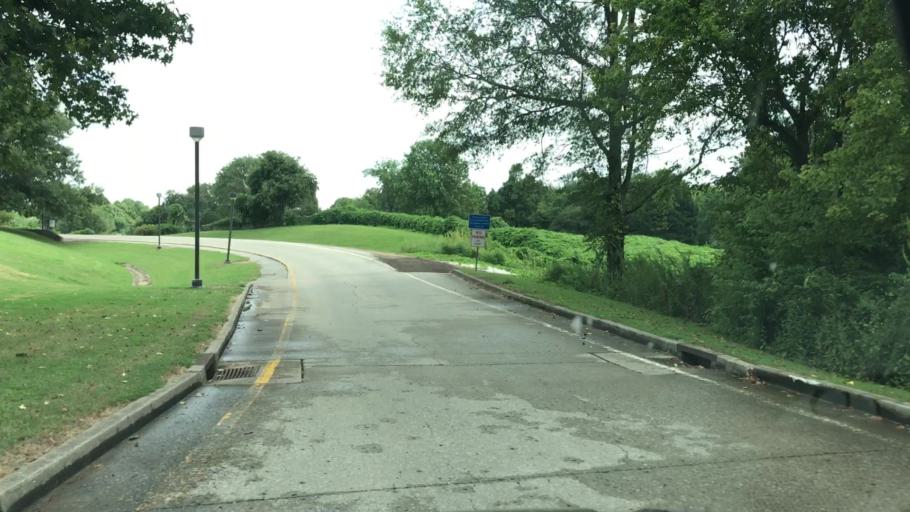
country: US
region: Tennessee
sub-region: Dyer County
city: Dyersburg
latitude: 36.0704
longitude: -89.4680
